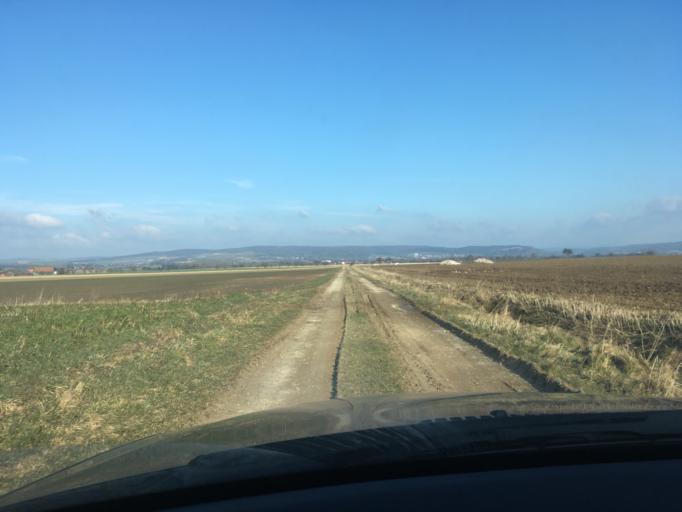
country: DE
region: Lower Saxony
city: Einbeck
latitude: 51.8008
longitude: 9.7946
